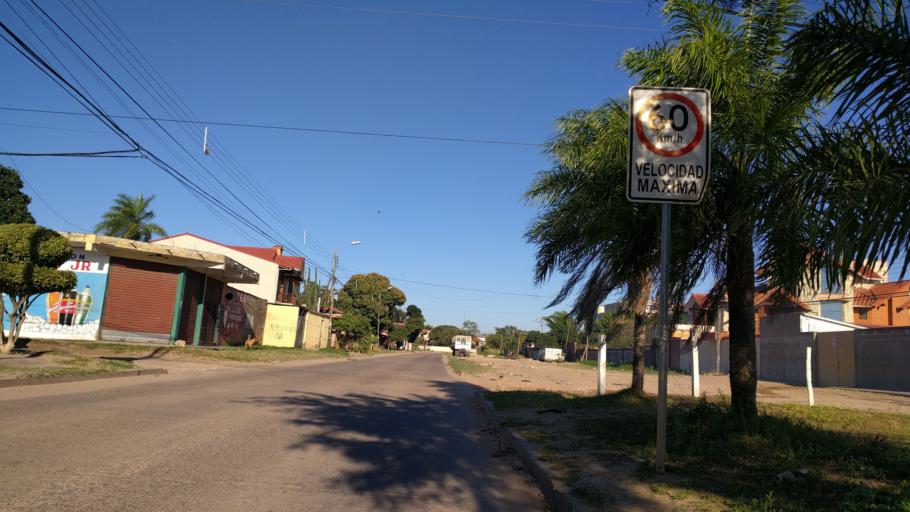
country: BO
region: Santa Cruz
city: Santa Cruz de la Sierra
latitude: -17.8030
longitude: -63.2186
